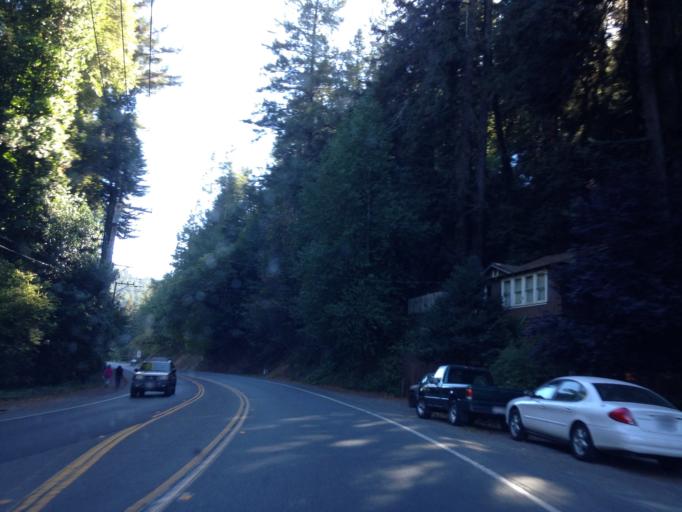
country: US
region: California
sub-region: Sonoma County
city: Guerneville
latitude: 38.5013
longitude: -123.0051
